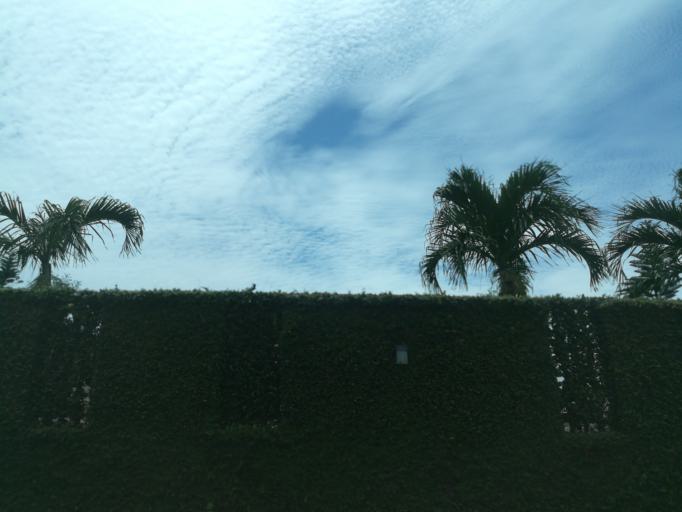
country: NG
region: Lagos
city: Ebute Ikorodu
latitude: 6.5798
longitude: 3.4890
